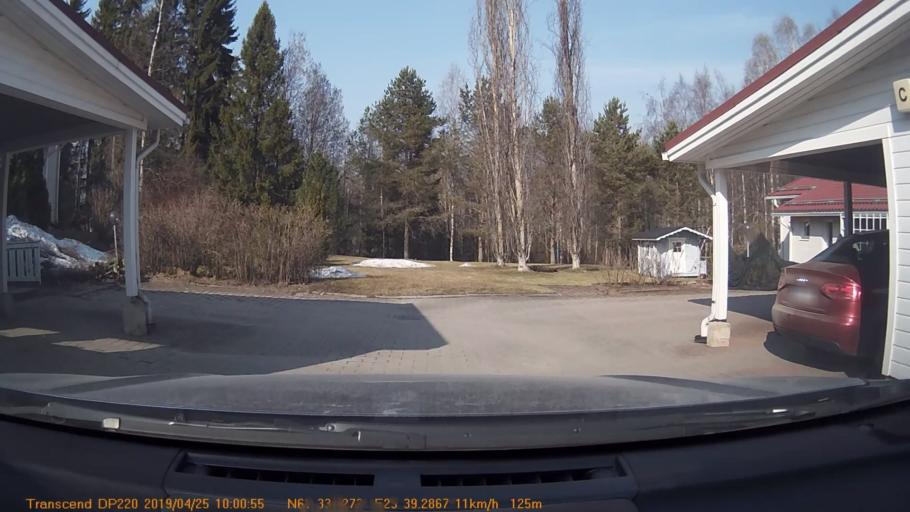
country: FI
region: Pirkanmaa
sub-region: Tampere
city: Yloejaervi
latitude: 61.5555
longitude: 23.6549
